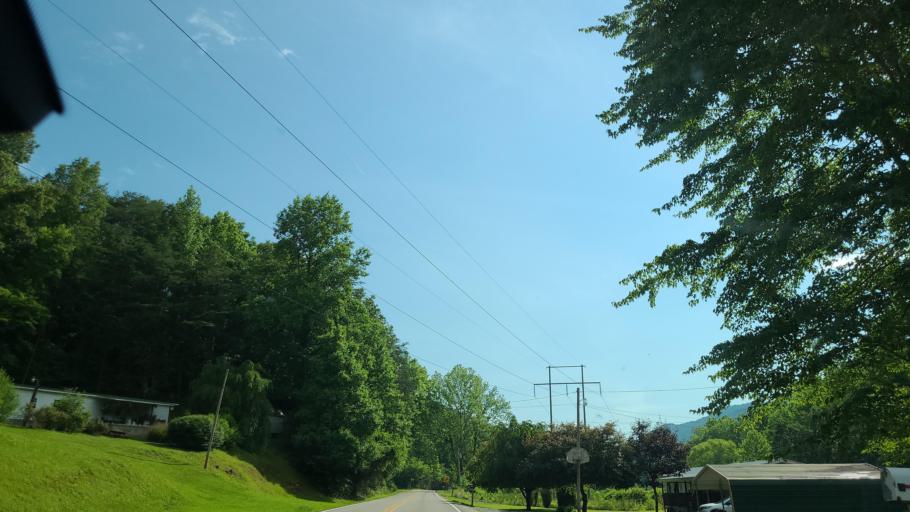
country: US
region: Kentucky
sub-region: Bell County
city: Pineville
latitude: 36.7045
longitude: -83.8415
